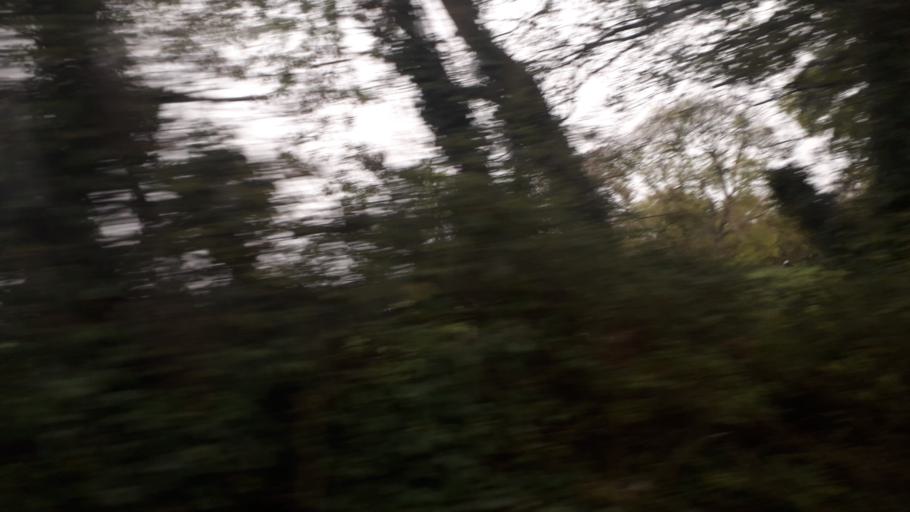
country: IE
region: Leinster
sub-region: Uibh Fhaili
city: Birr
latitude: 52.9721
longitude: -8.0029
